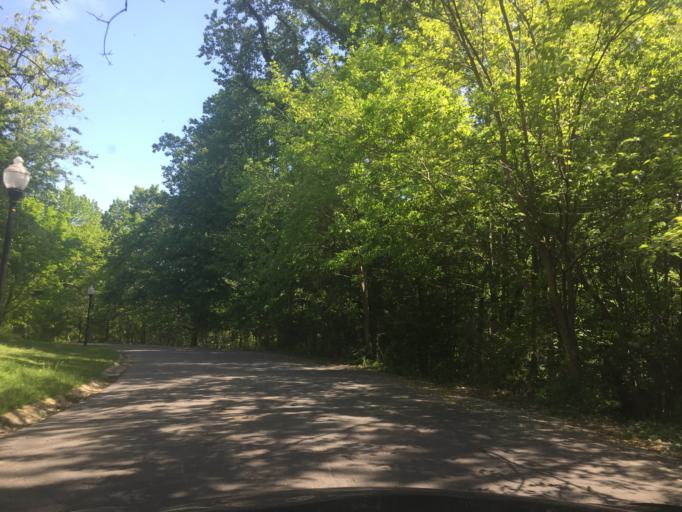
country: US
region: Maryland
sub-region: City of Baltimore
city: Baltimore
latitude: 39.3223
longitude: -76.6429
